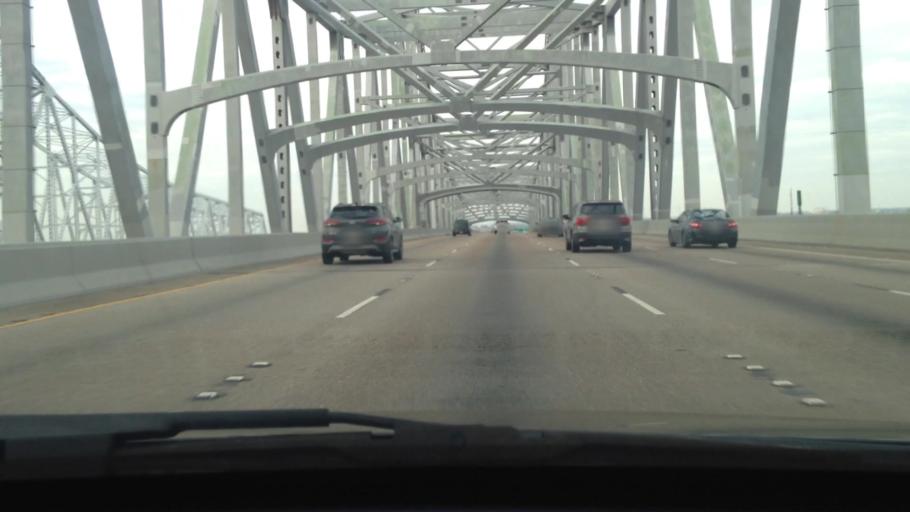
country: US
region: Louisiana
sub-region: Orleans Parish
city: New Orleans
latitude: 29.9389
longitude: -90.0569
